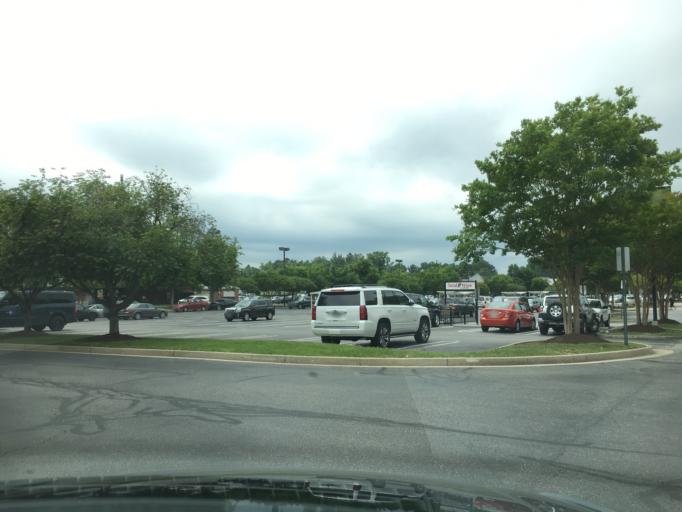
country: US
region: Virginia
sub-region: Henrico County
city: Short Pump
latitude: 37.6497
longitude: -77.6149
